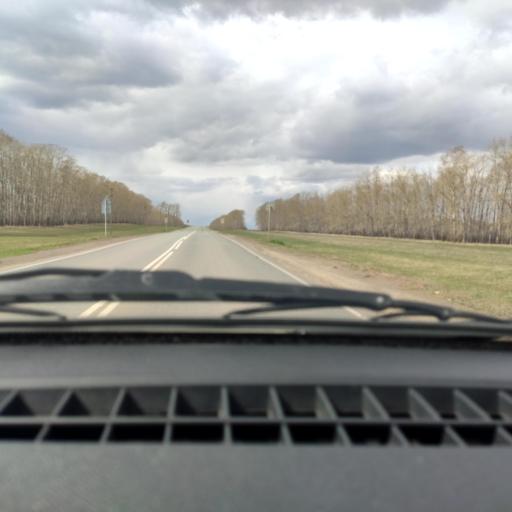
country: RU
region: Bashkortostan
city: Alekseyevka
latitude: 55.0556
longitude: 55.1188
